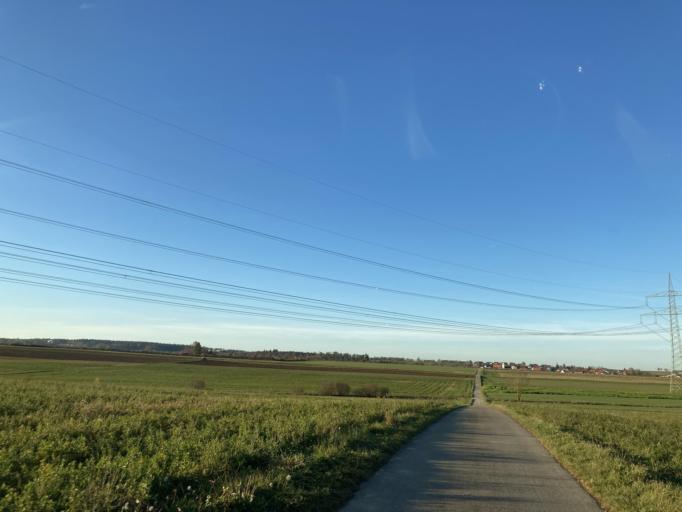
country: DE
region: Baden-Wuerttemberg
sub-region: Tuebingen Region
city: Hirrlingen
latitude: 48.4182
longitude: 8.8804
